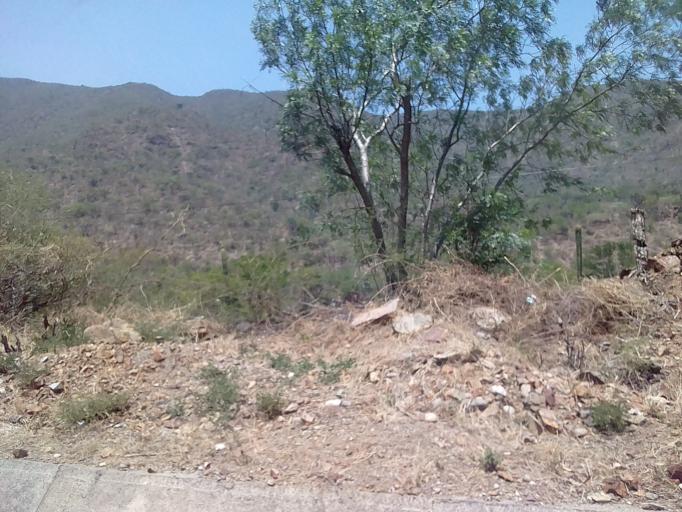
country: MX
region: Oaxaca
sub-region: San Pedro Quiatoni
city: San Pedro Quiatoni
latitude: 16.6692
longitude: -96.1412
